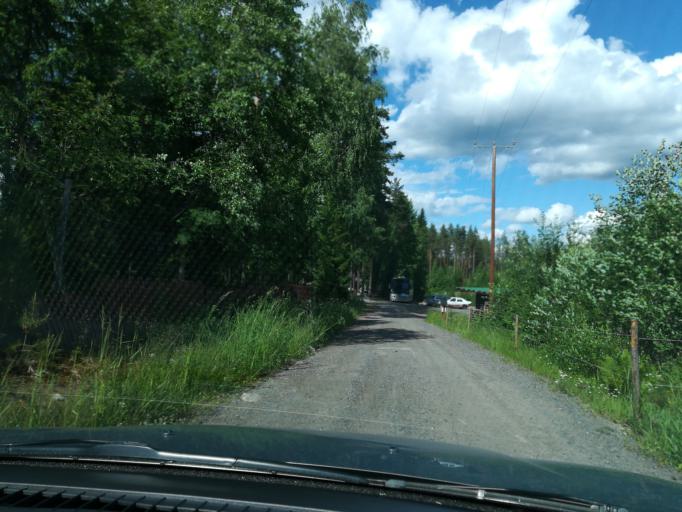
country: FI
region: Southern Savonia
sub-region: Mikkeli
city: Hirvensalmi
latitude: 61.6602
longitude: 27.0036
